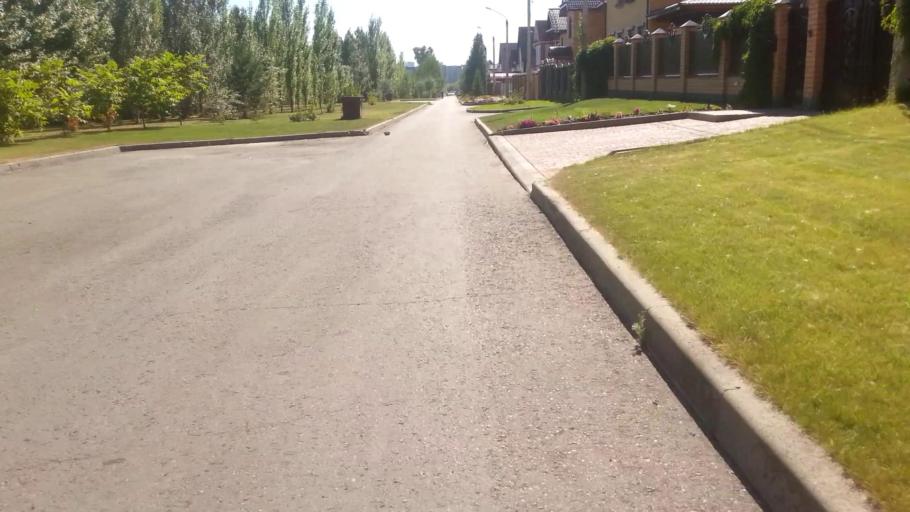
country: RU
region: Altai Krai
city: Novosilikatnyy
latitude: 53.3541
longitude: 83.6555
